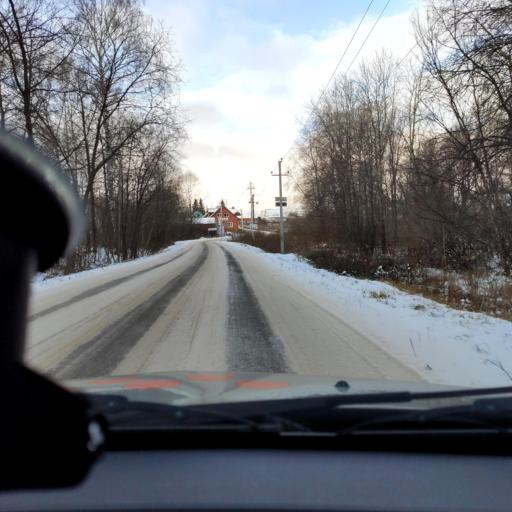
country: RU
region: Bashkortostan
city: Avdon
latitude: 54.7831
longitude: 55.7379
